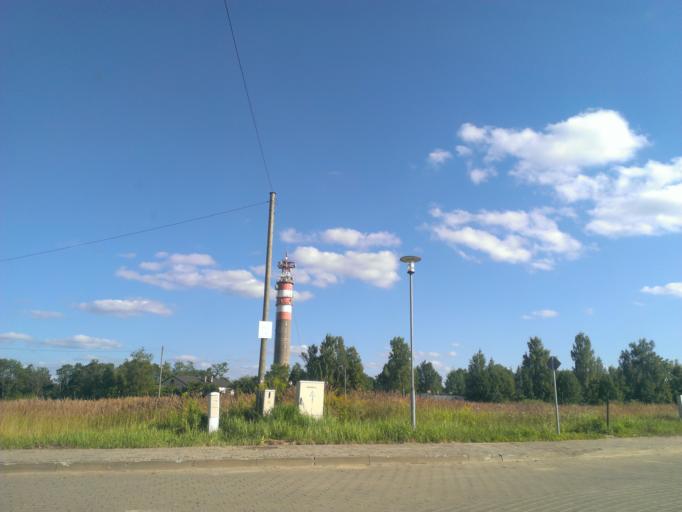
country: LV
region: Sigulda
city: Sigulda
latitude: 57.1665
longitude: 24.8775
